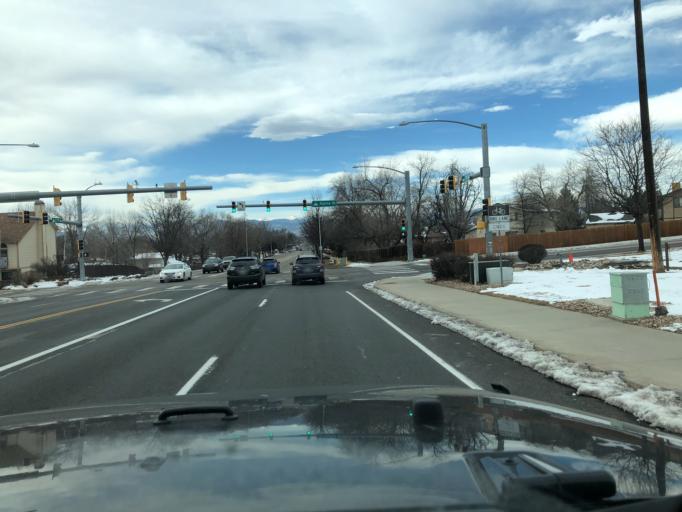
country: US
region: Colorado
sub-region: Boulder County
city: Longmont
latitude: 40.1741
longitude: -105.0824
